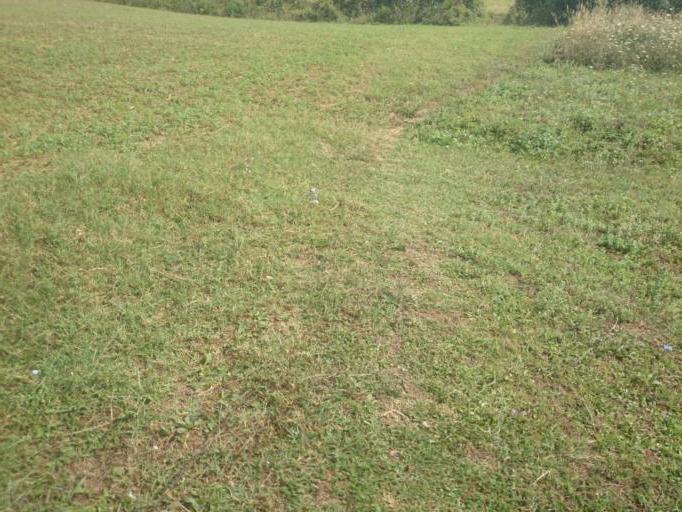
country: AL
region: Elbasan
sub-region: Rrethi i Elbasanit
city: Zavaline
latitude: 40.9501
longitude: 20.2358
